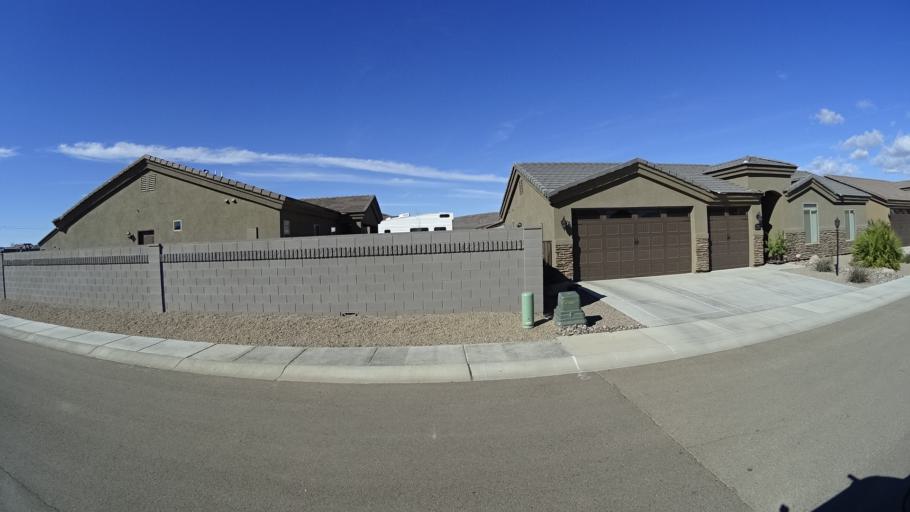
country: US
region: Arizona
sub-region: Mohave County
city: New Kingman-Butler
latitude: 35.2333
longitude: -114.0206
